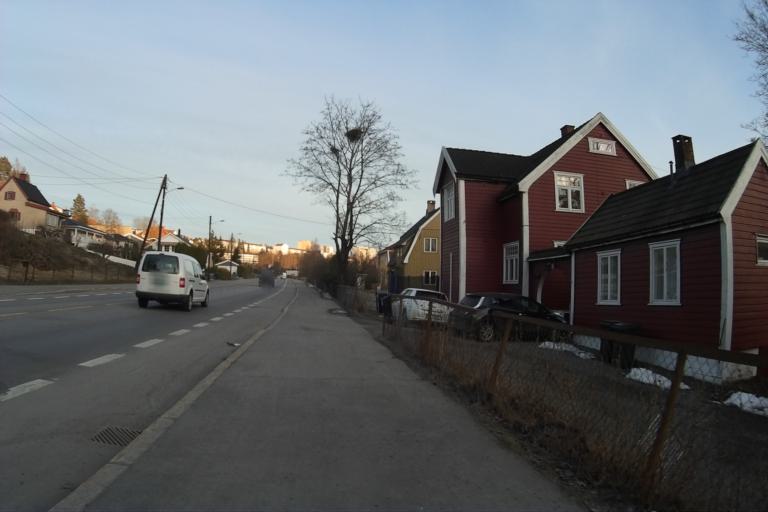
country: NO
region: Oslo
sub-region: Oslo
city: Oslo
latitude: 59.9005
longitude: 10.8263
